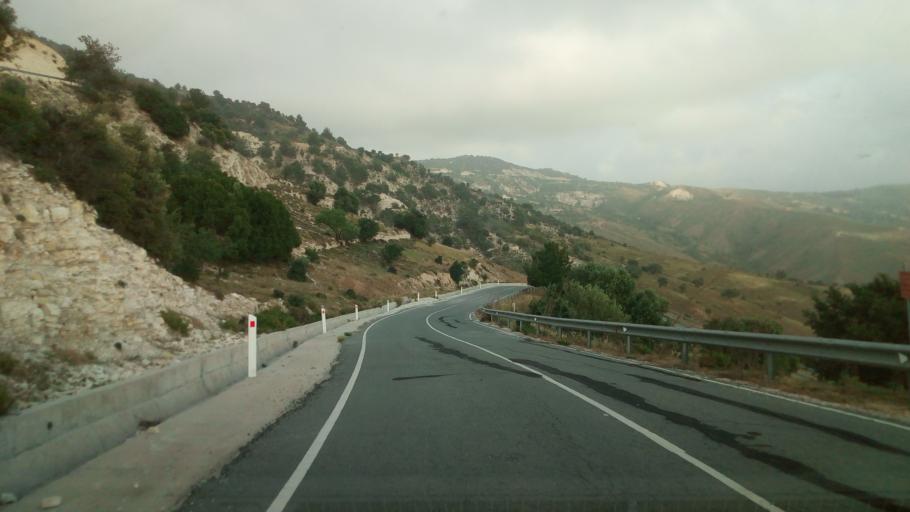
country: CY
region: Limassol
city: Pachna
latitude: 34.8399
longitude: 32.6727
